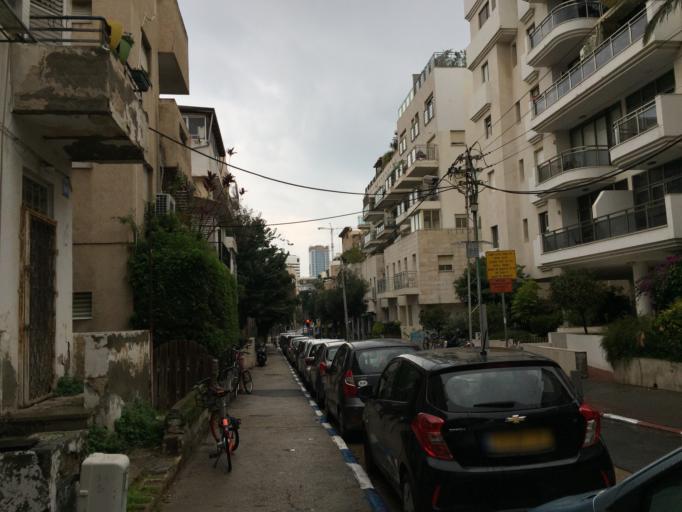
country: IL
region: Tel Aviv
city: Tel Aviv
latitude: 32.0713
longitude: 34.7742
